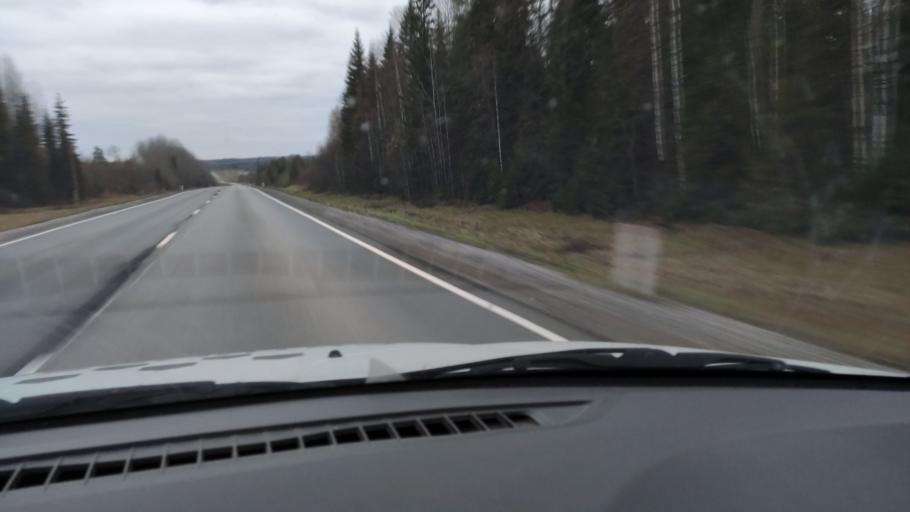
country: RU
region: Kirov
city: Lesnyye Polyany
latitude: 58.8236
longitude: 52.7524
